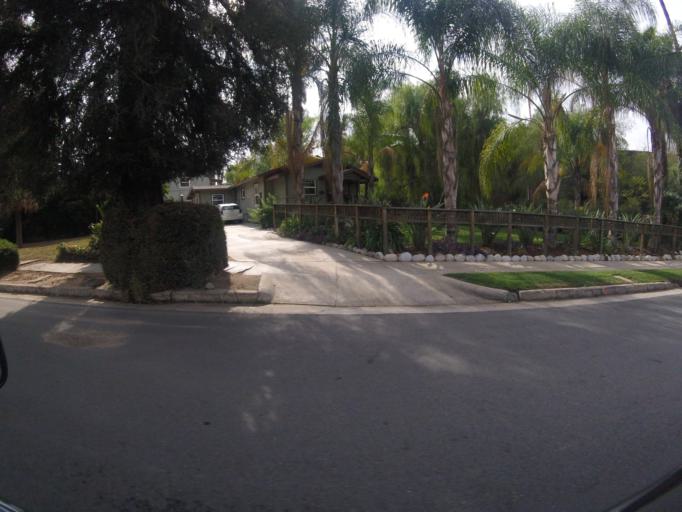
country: US
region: California
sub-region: San Bernardino County
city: Redlands
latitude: 34.0555
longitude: -117.1635
